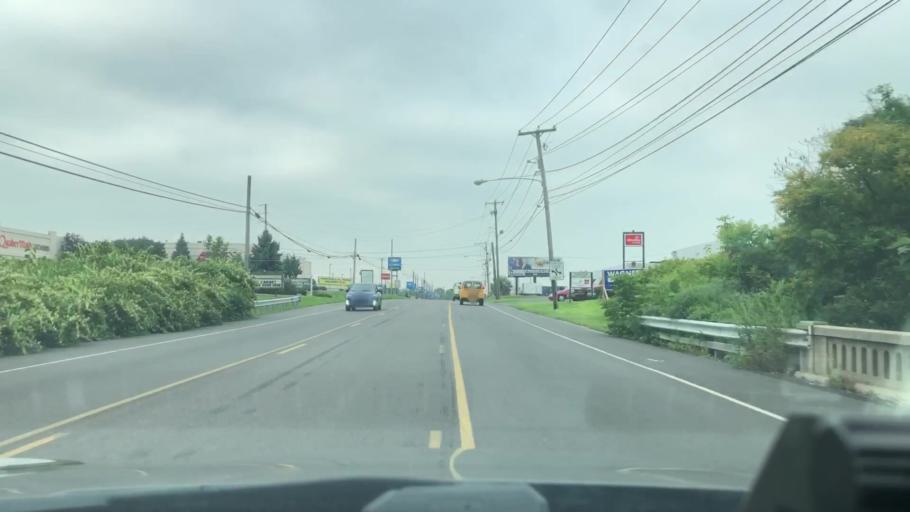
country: US
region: Pennsylvania
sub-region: Berks County
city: Muhlenberg Park
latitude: 40.4003
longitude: -75.9360
